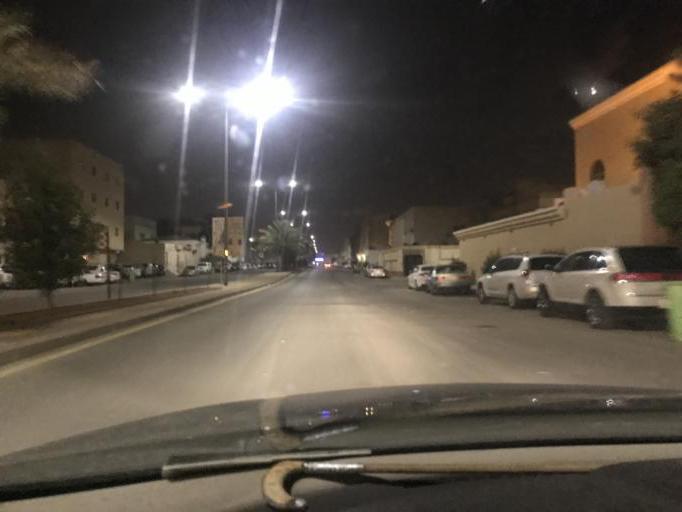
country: SA
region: Ar Riyad
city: Riyadh
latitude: 24.7322
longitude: 46.7796
